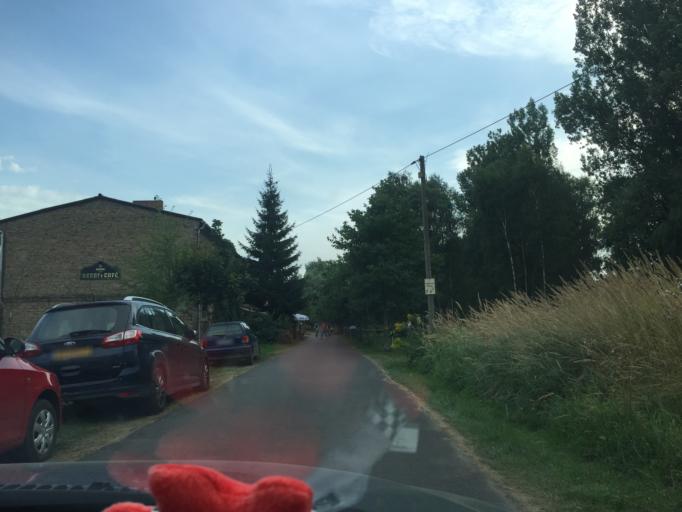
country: DE
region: Brandenburg
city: Zehdenick
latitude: 53.0287
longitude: 13.3114
